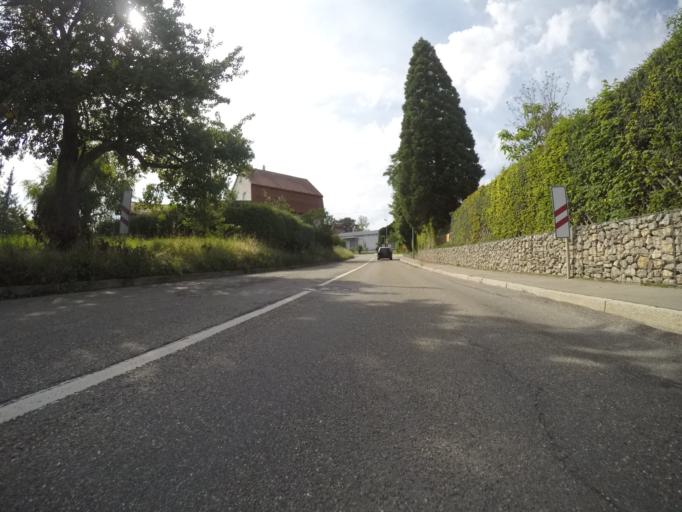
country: DE
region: Baden-Wuerttemberg
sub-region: Regierungsbezirk Stuttgart
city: Eberdingen
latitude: 48.8513
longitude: 8.9884
